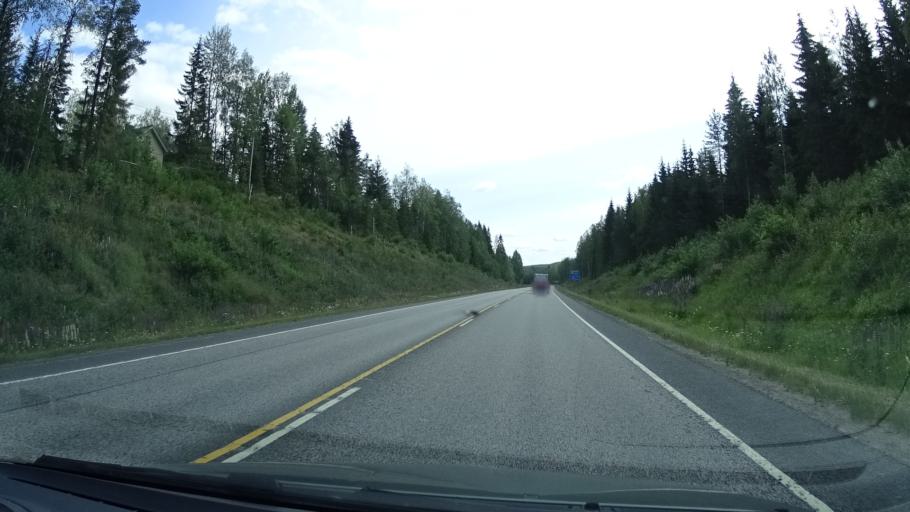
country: FI
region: Central Finland
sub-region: Jyvaeskylae
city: Jyvaeskylae
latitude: 62.2637
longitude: 25.5858
